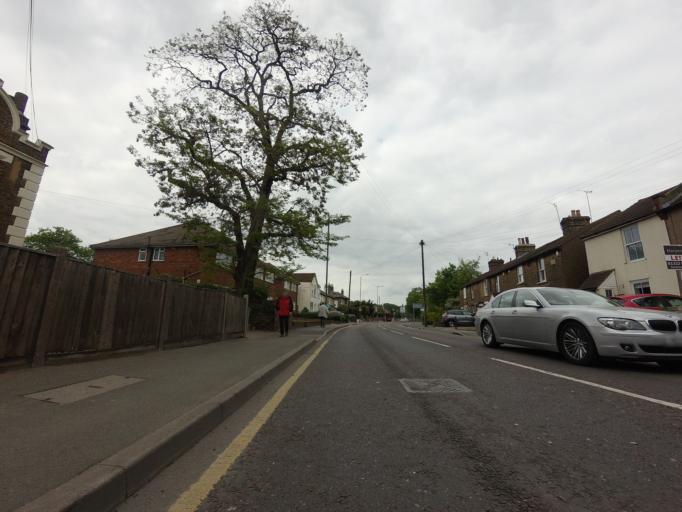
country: GB
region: England
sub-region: Greater London
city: Bexley
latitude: 51.4440
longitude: 0.1517
